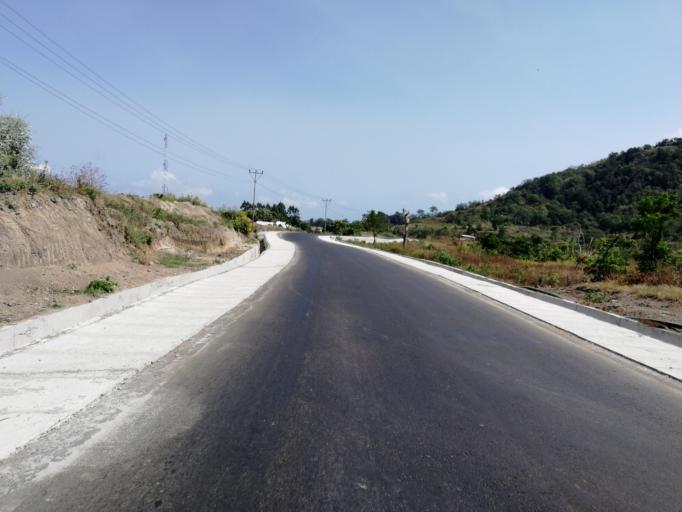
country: ID
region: West Nusa Tenggara
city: Sembalunlawang
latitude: -8.3497
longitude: 116.5091
